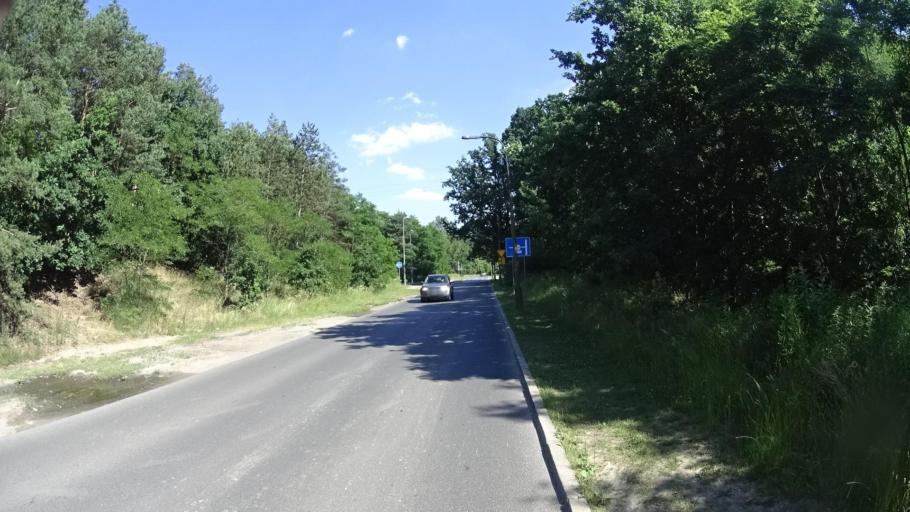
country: PL
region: Masovian Voivodeship
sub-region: Warszawa
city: Bialoleka
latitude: 52.3513
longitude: 20.9698
